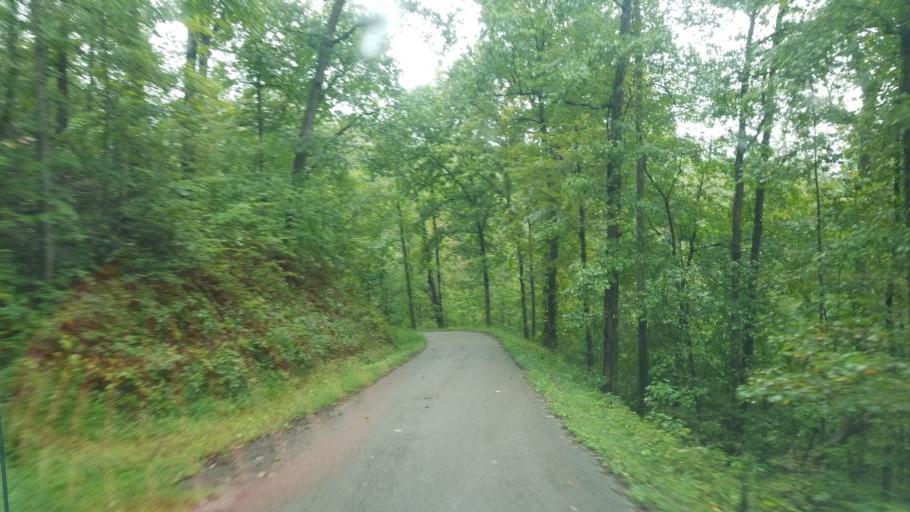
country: US
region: Ohio
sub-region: Scioto County
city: West Portsmouth
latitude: 38.7700
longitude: -83.1422
